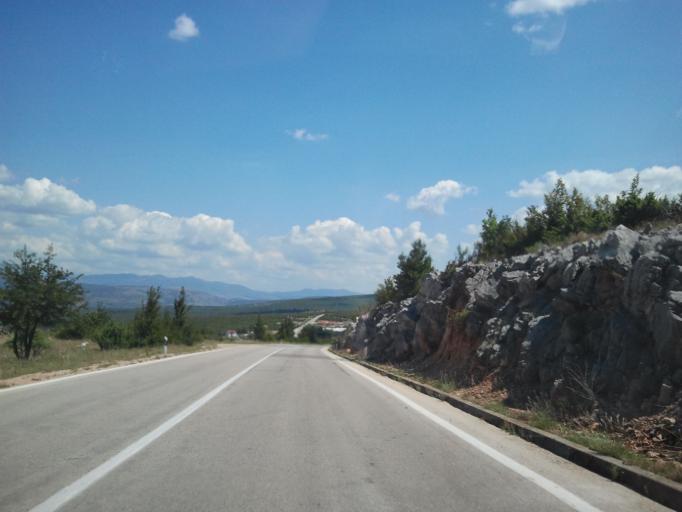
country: HR
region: Zadarska
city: Obrovac
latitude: 44.1957
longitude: 15.6707
